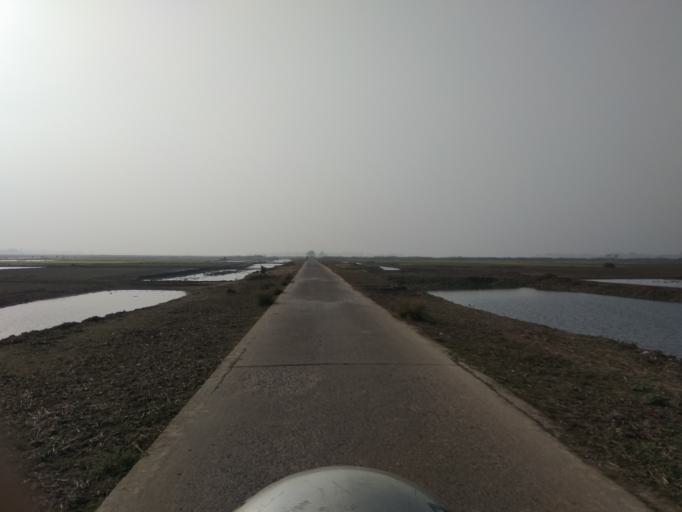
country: BD
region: Rajshahi
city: Ishurdi
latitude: 24.4824
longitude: 89.2260
